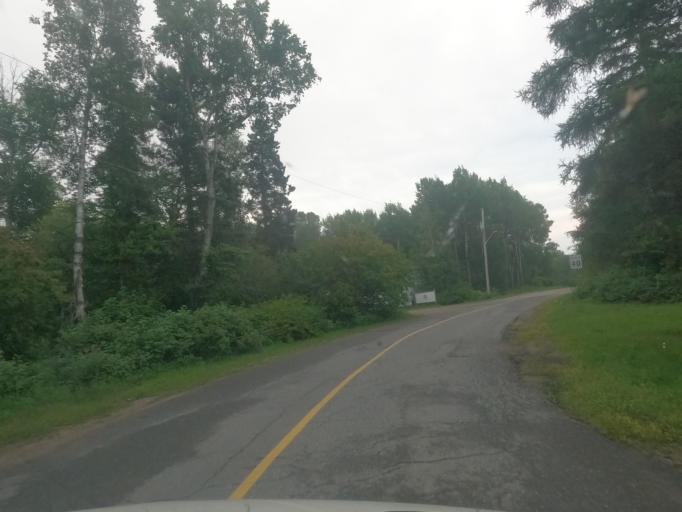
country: CA
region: Ontario
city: Marathon
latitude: 48.7796
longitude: -87.1022
